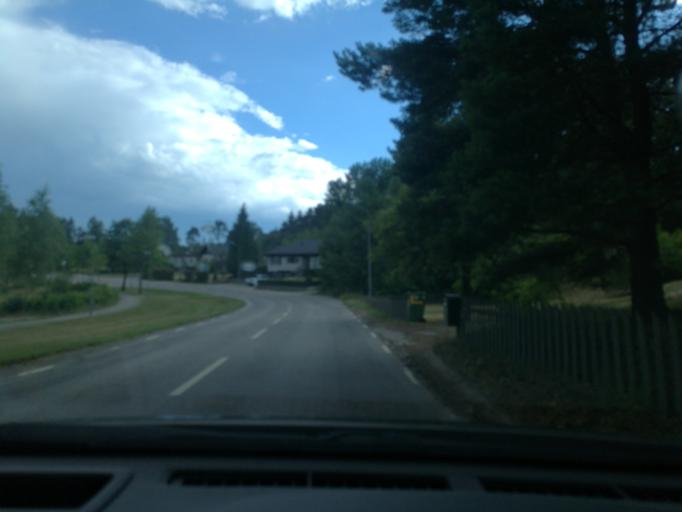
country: SE
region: Soedermanland
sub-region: Eskilstuna Kommun
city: Arla
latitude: 59.3845
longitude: 16.6764
